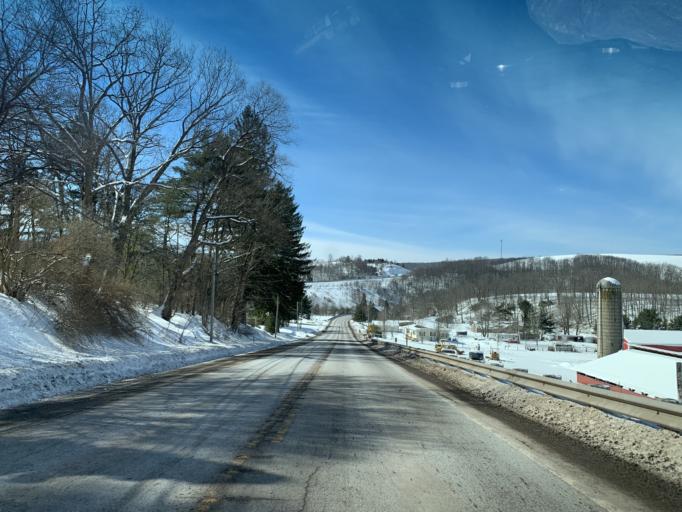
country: US
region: Pennsylvania
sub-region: Somerset County
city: Meyersdale
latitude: 39.6971
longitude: -79.1688
